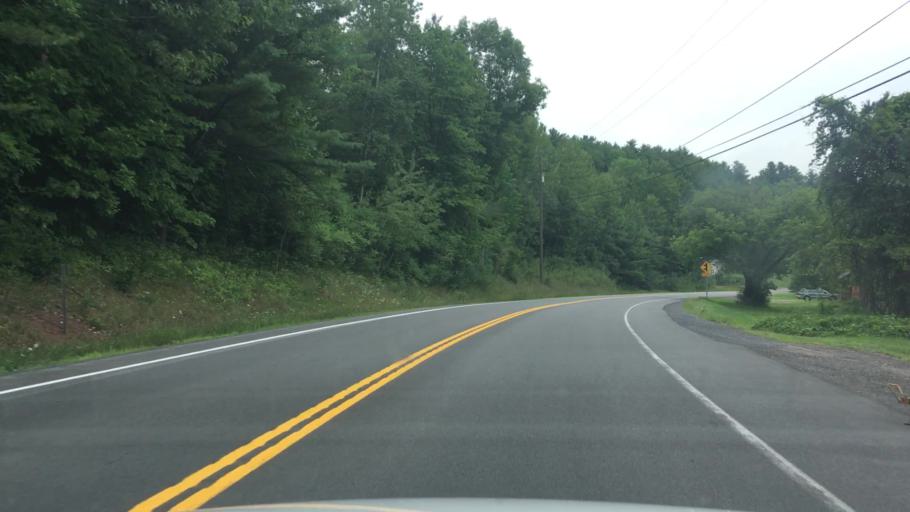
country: US
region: New York
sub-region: Essex County
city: Keeseville
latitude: 44.4762
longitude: -73.5692
